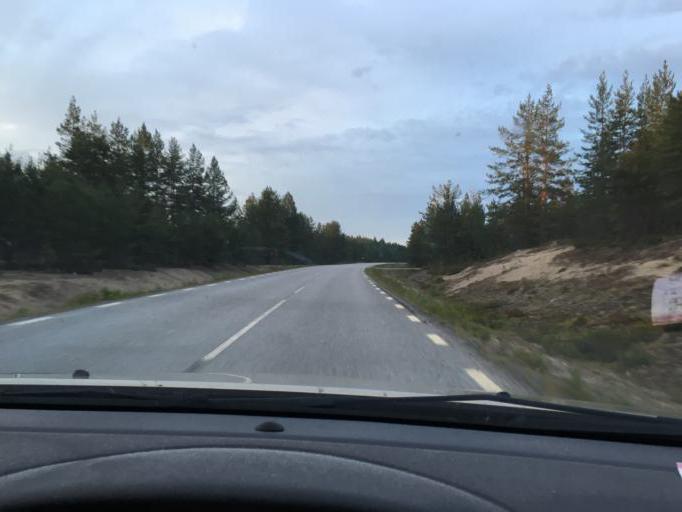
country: SE
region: Norrbotten
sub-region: Lulea Kommun
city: Ranea
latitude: 66.0488
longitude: 22.2473
